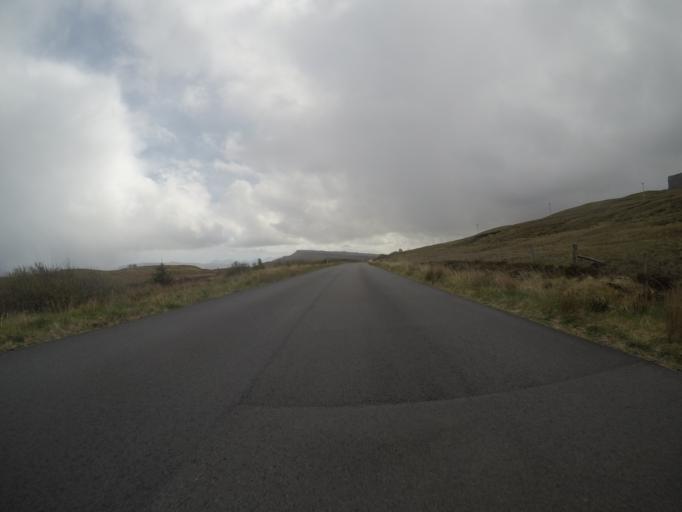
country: GB
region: Scotland
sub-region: Highland
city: Portree
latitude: 57.5079
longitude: -6.1512
